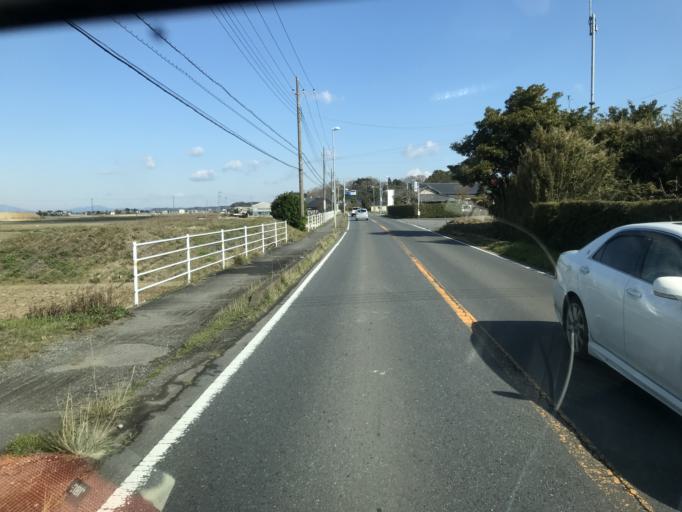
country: JP
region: Ibaraki
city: Itako
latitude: 36.0120
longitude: 140.4696
